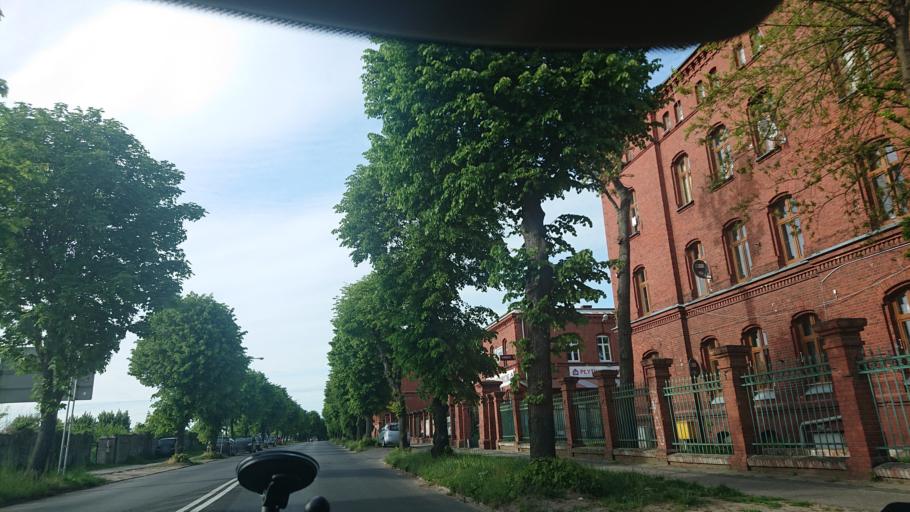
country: PL
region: Greater Poland Voivodeship
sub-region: Powiat gnieznienski
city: Gniezno
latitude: 52.5145
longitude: 17.5953
